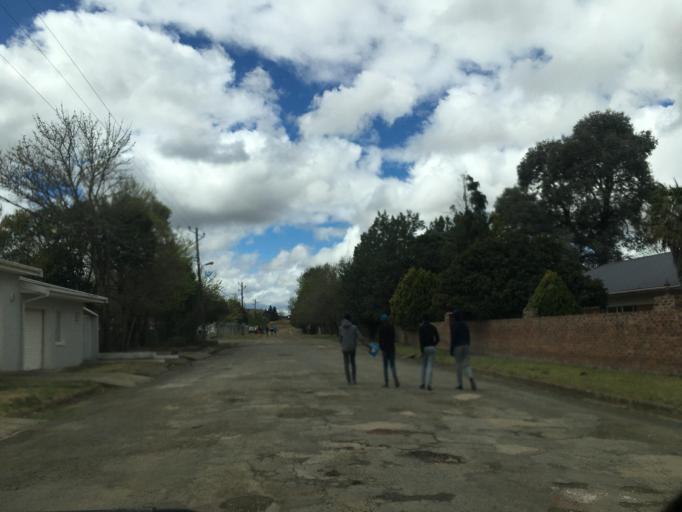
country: ZA
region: Eastern Cape
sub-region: Chris Hani District Municipality
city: Elliot
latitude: -31.3294
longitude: 27.8540
